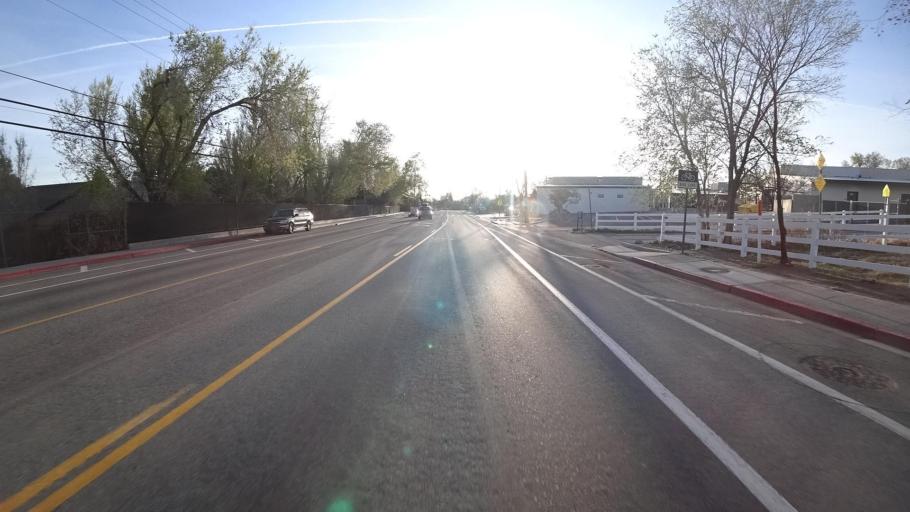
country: US
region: Nevada
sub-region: Washoe County
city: Reno
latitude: 39.5073
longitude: -119.8615
